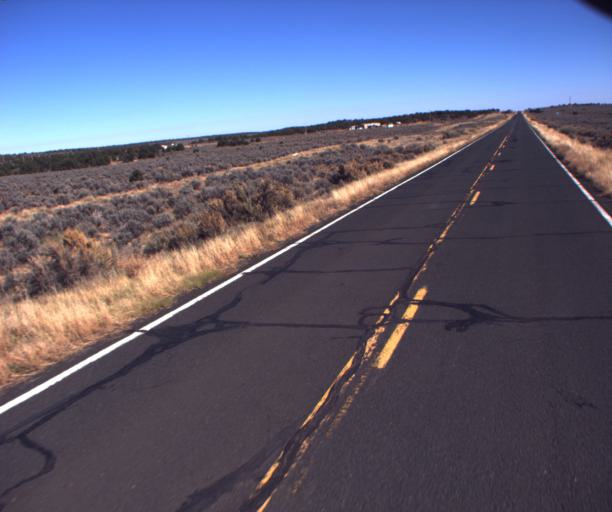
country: US
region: Arizona
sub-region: Navajo County
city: First Mesa
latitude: 35.7362
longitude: -110.0890
